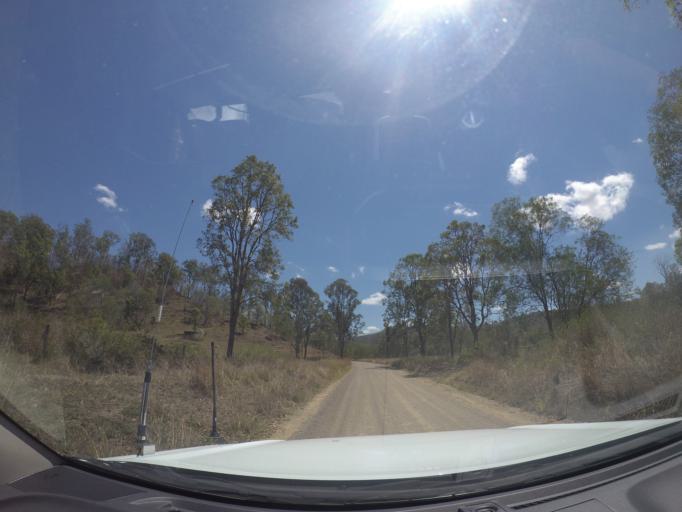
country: AU
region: Queensland
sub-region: Ipswich
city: Springfield Lakes
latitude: -27.8203
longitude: 152.8577
